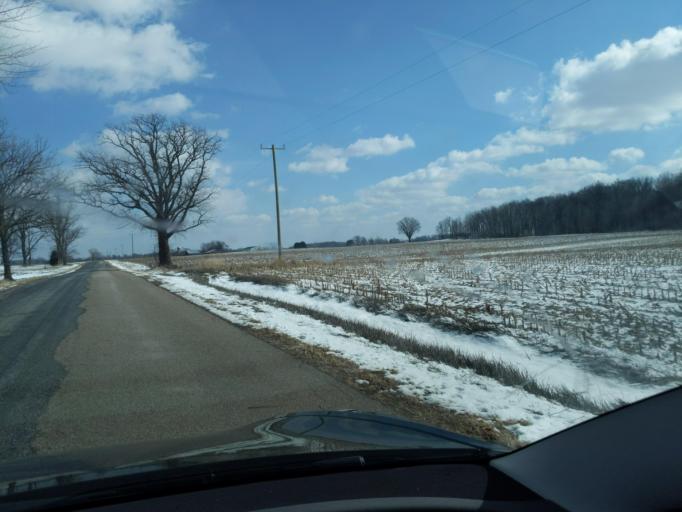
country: US
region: Michigan
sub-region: Ingham County
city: Webberville
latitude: 42.6151
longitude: -84.2058
